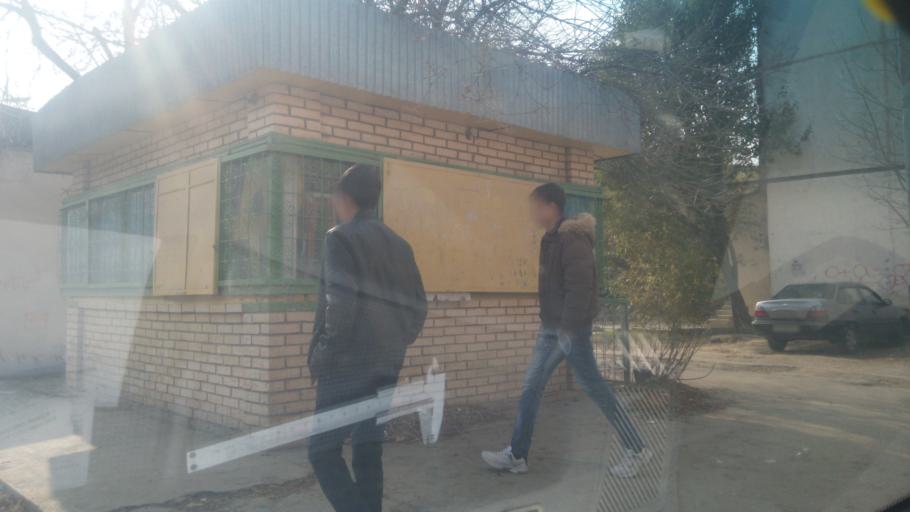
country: UZ
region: Sirdaryo
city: Guliston
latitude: 40.5140
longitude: 68.7716
